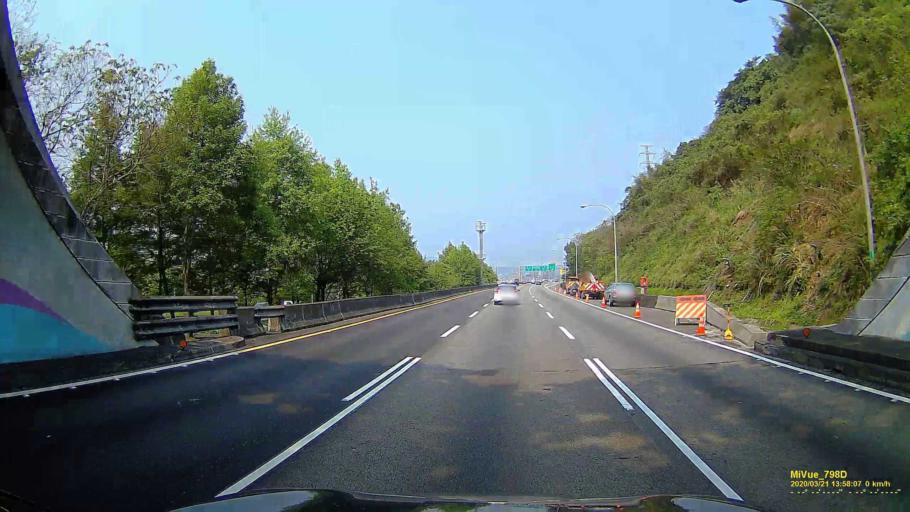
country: TW
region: Taipei
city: Taipei
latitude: 24.9707
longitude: 121.5515
